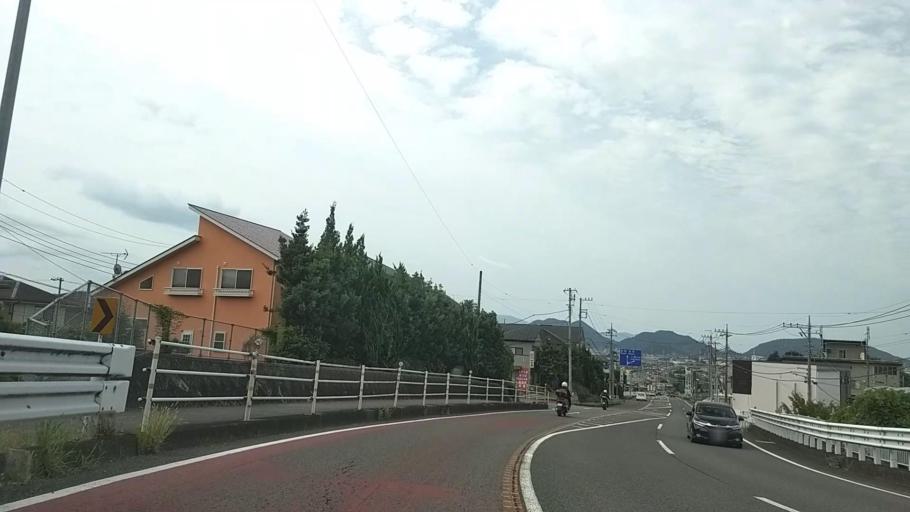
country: JP
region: Shizuoka
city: Mishima
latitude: 35.1226
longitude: 138.9337
